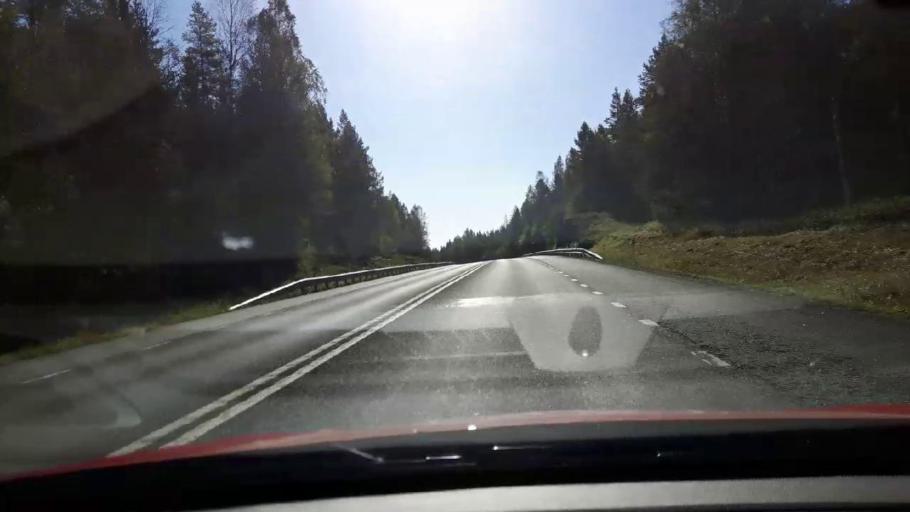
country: SE
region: Jaemtland
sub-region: Braecke Kommun
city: Braecke
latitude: 62.6931
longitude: 15.5393
